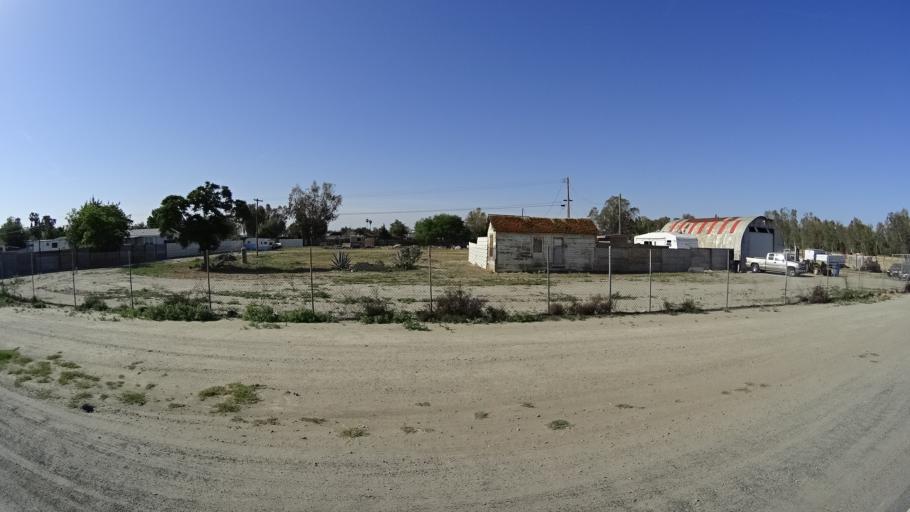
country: US
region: California
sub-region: Kings County
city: Corcoran
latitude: 36.0981
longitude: -119.5916
